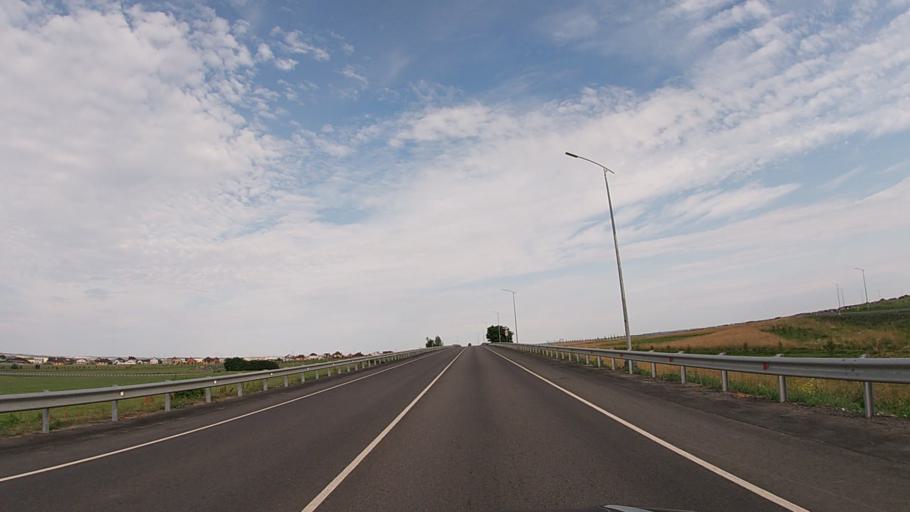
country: RU
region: Belgorod
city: Severnyy
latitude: 50.6739
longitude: 36.4757
